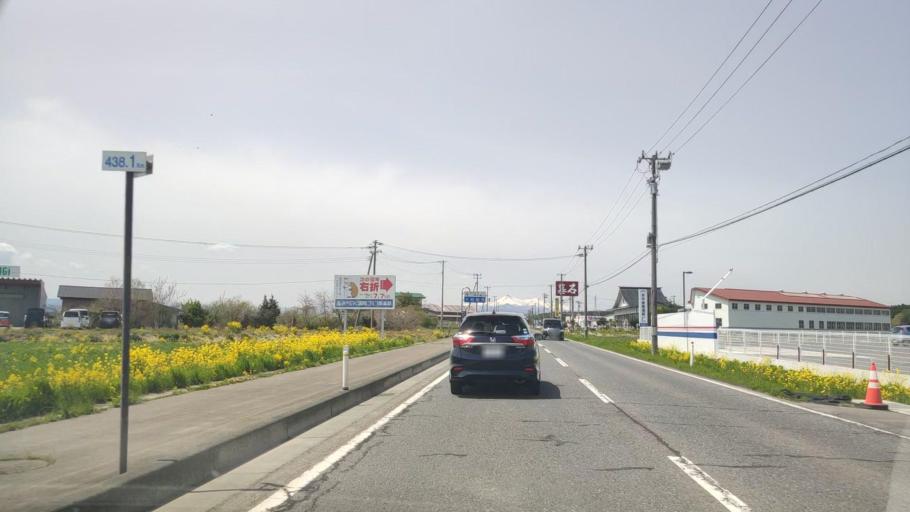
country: JP
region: Aomori
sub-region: Misawa Shi
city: Inuotose
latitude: 40.6110
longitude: 141.2715
